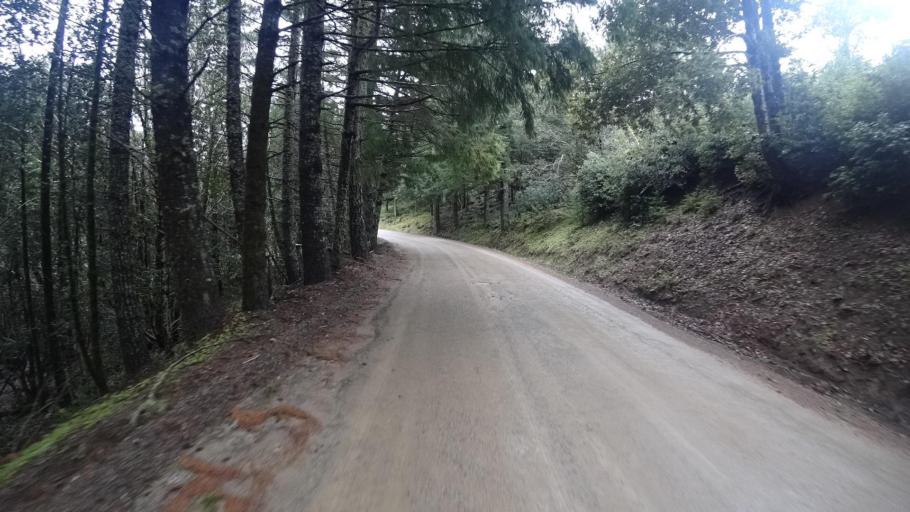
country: US
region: California
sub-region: Humboldt County
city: Westhaven-Moonstone
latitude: 41.1402
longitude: -123.8602
